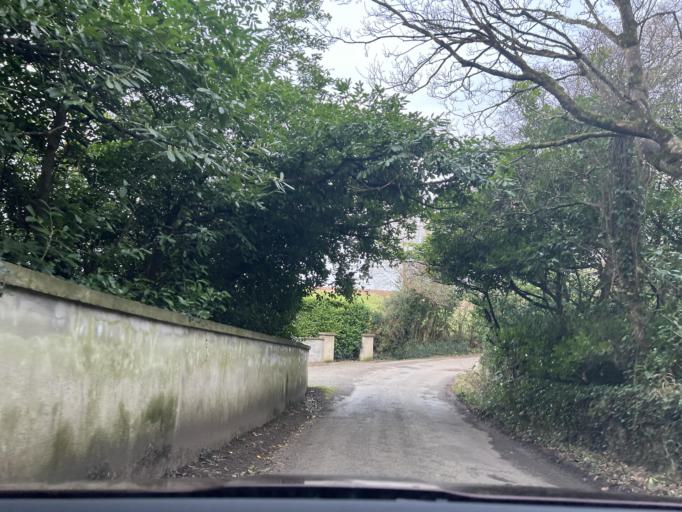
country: IE
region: Leinster
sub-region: Loch Garman
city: Loch Garman
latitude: 52.3726
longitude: -6.5395
